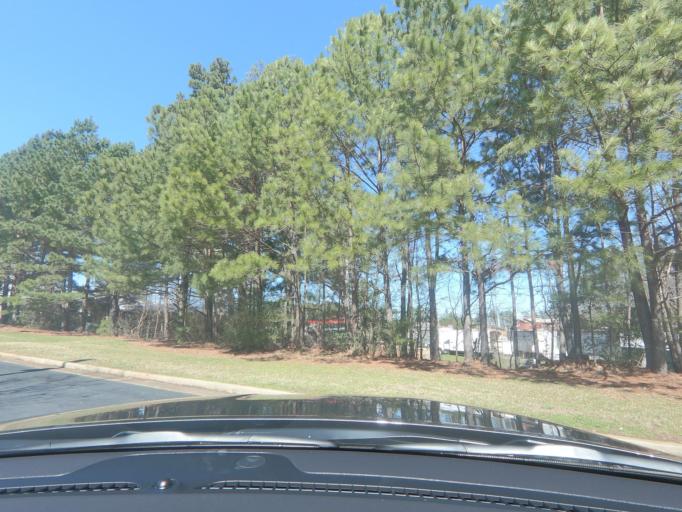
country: US
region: Georgia
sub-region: Fulton County
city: Milton
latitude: 34.1526
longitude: -84.2506
